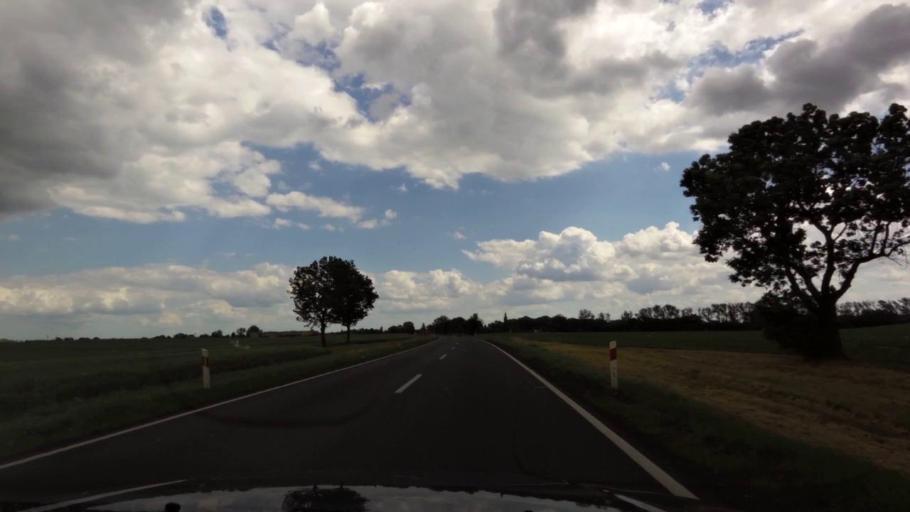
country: PL
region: West Pomeranian Voivodeship
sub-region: Powiat mysliborski
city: Mysliborz
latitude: 52.9544
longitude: 14.7742
